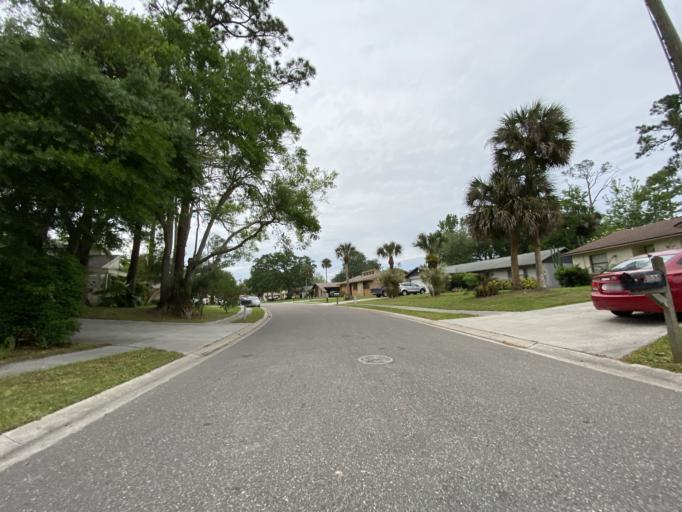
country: US
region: Florida
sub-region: Volusia County
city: South Daytona
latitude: 29.1529
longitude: -80.9999
